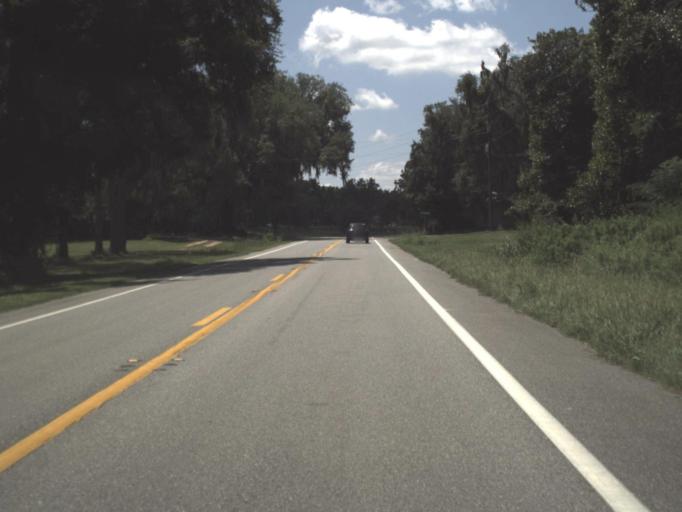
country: US
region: Florida
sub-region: Madison County
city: Madison
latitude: 30.5320
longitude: -83.6319
